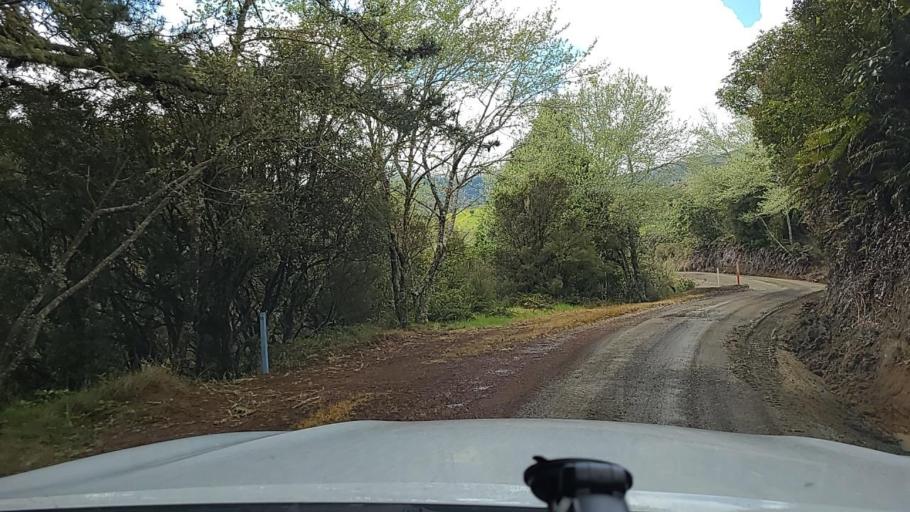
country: NZ
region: Bay of Plenty
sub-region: Opotiki District
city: Opotiki
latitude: -38.2506
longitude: 177.5979
